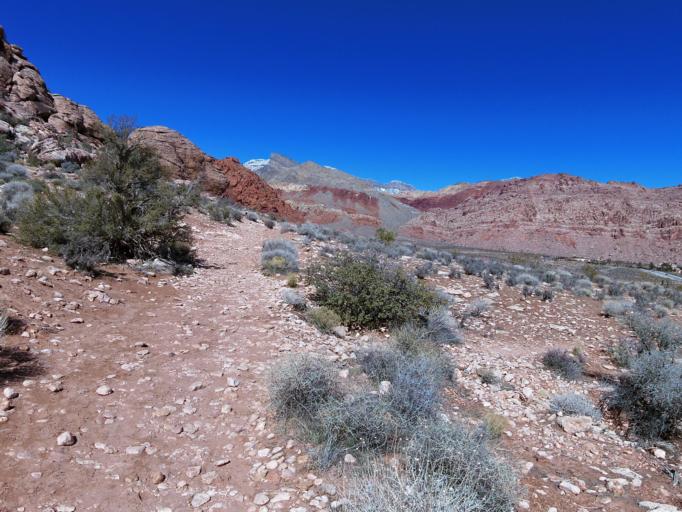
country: US
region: Nevada
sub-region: Clark County
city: Summerlin South
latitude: 36.1477
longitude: -115.4215
